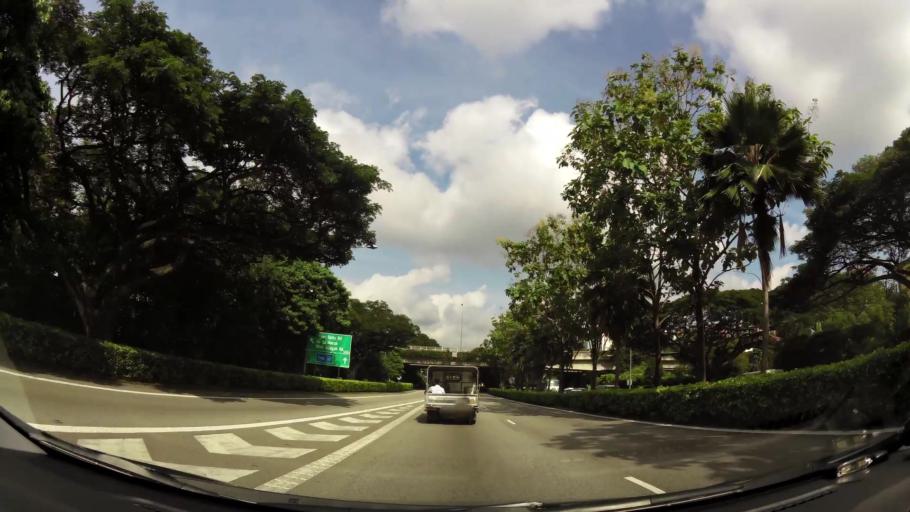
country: SG
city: Singapore
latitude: 1.2745
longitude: 103.8296
